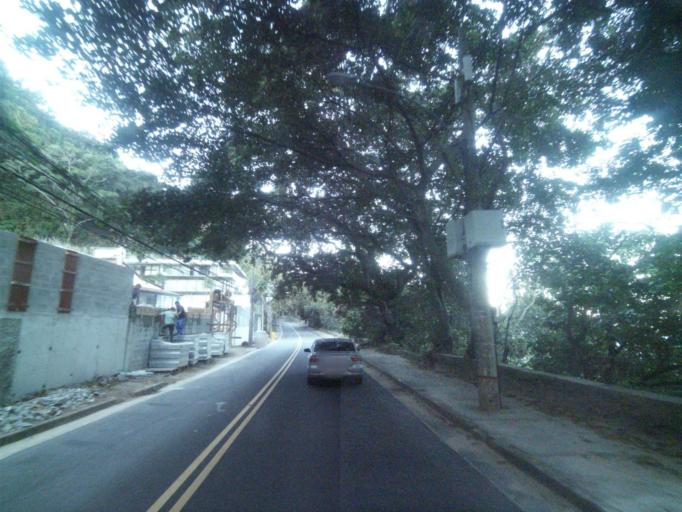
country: BR
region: Rio de Janeiro
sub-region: Rio De Janeiro
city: Rio de Janeiro
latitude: -23.0072
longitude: -43.2858
